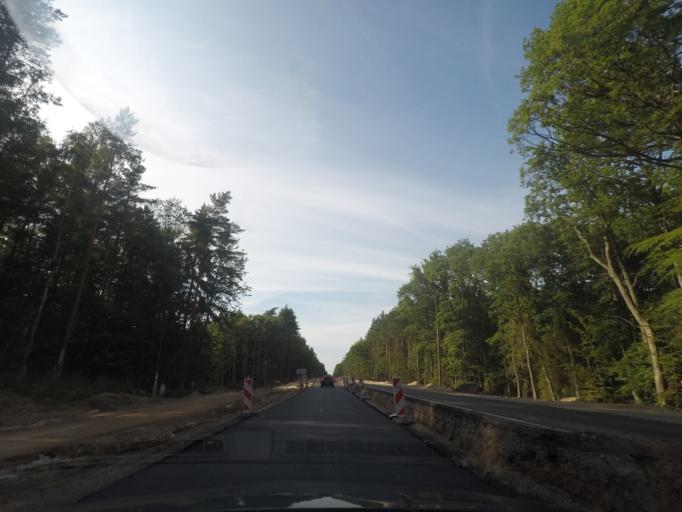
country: PL
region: Pomeranian Voivodeship
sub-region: Powiat leborski
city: Leba
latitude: 54.7011
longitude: 17.5869
